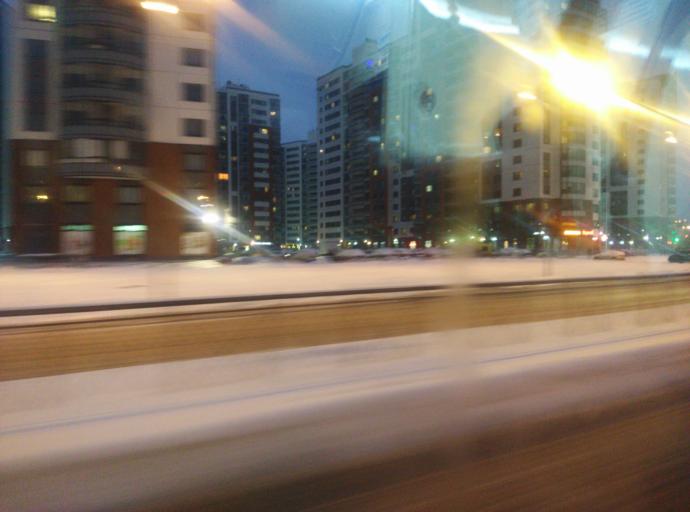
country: RU
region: St.-Petersburg
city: Komendantsky aerodrom
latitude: 60.0189
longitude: 30.2674
